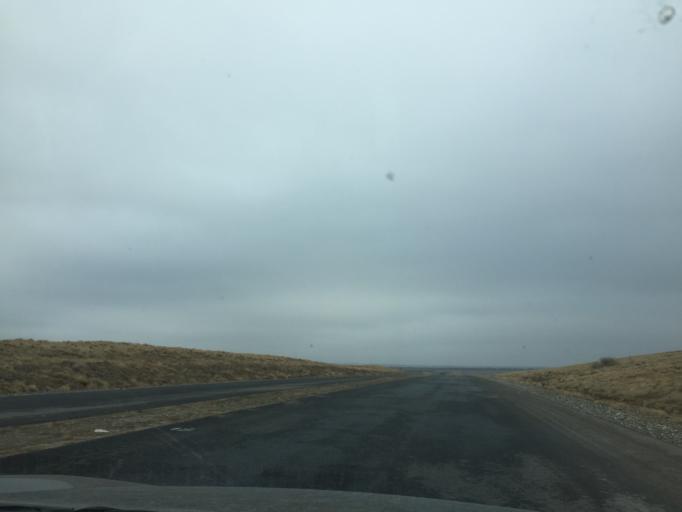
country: KZ
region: Ongtustik Qazaqstan
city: Kokterek
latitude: 42.5445
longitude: 70.1843
